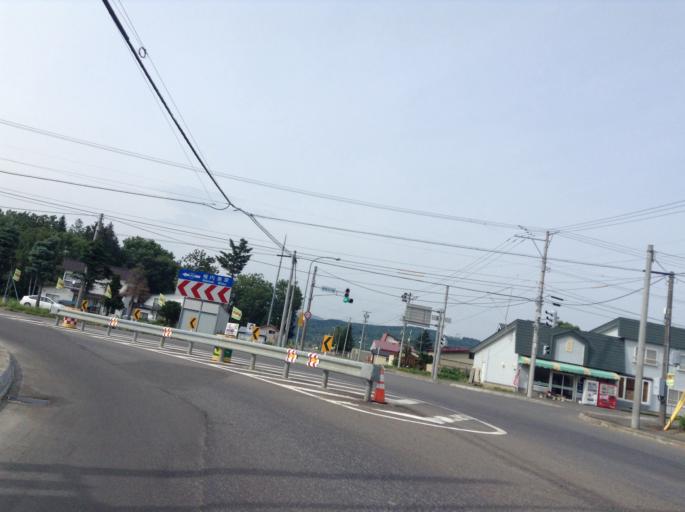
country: JP
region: Hokkaido
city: Nayoro
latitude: 44.4366
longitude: 142.4033
